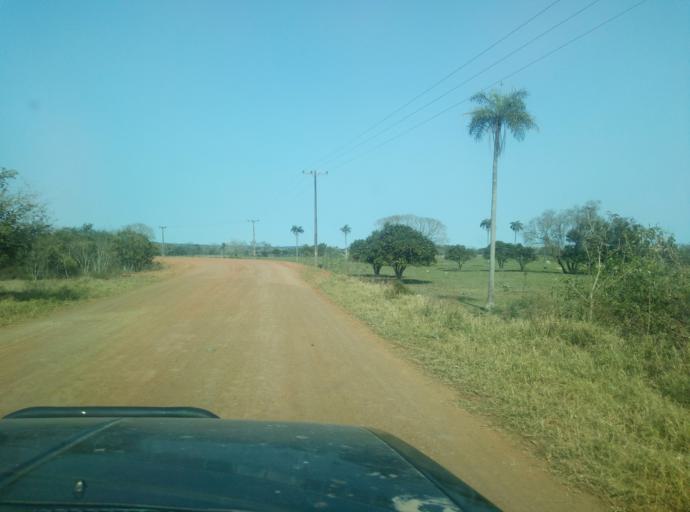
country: PY
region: Caaguazu
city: Coronel Oviedo
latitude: -25.3417
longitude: -56.3162
